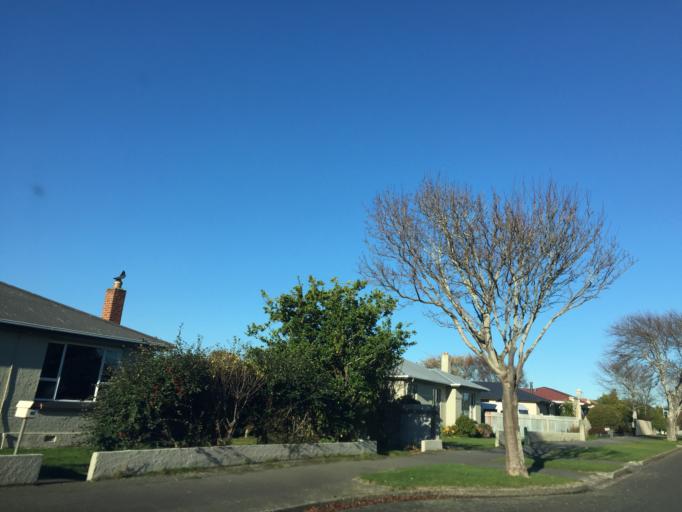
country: NZ
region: Southland
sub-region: Invercargill City
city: Invercargill
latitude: -46.4048
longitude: 168.3717
